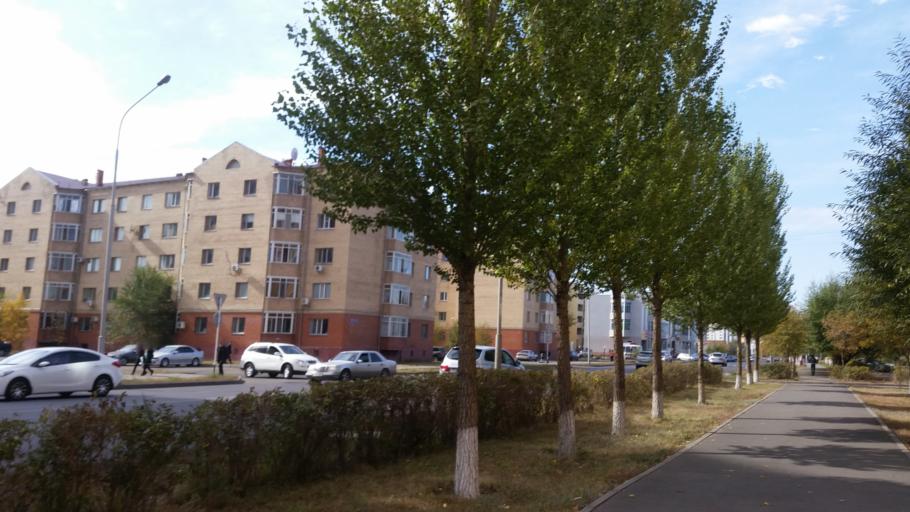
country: KZ
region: Astana Qalasy
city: Astana
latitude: 51.1605
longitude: 71.4889
